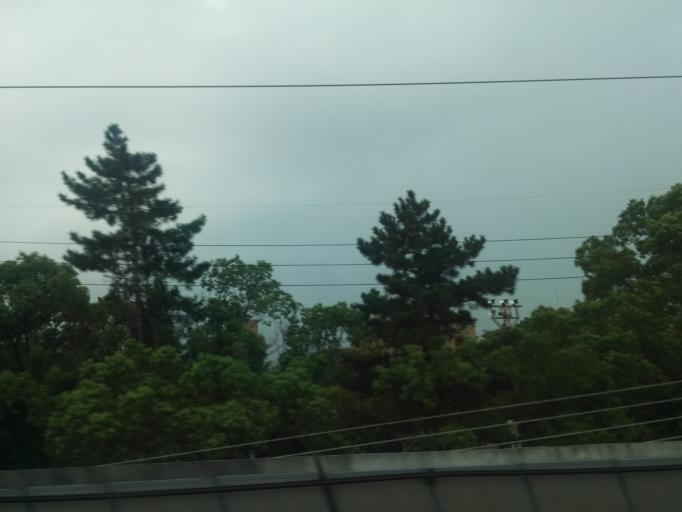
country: JP
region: Aichi
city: Nagoya-shi
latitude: 35.1339
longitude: 136.8857
